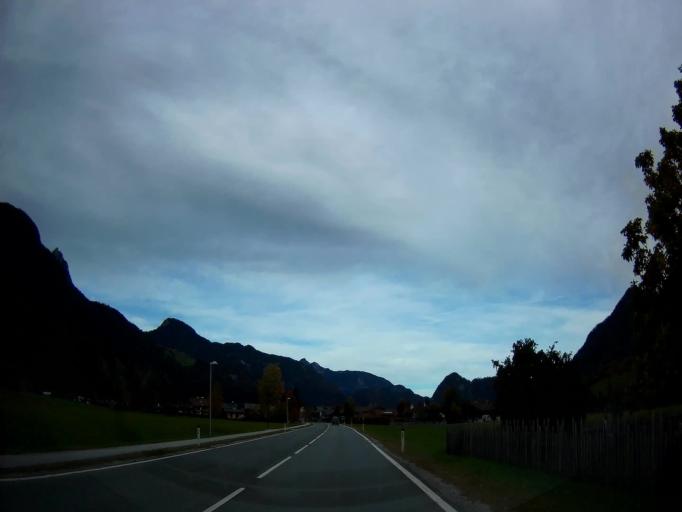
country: AT
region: Salzburg
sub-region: Politischer Bezirk Zell am See
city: Lofer
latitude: 47.5776
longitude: 12.6992
